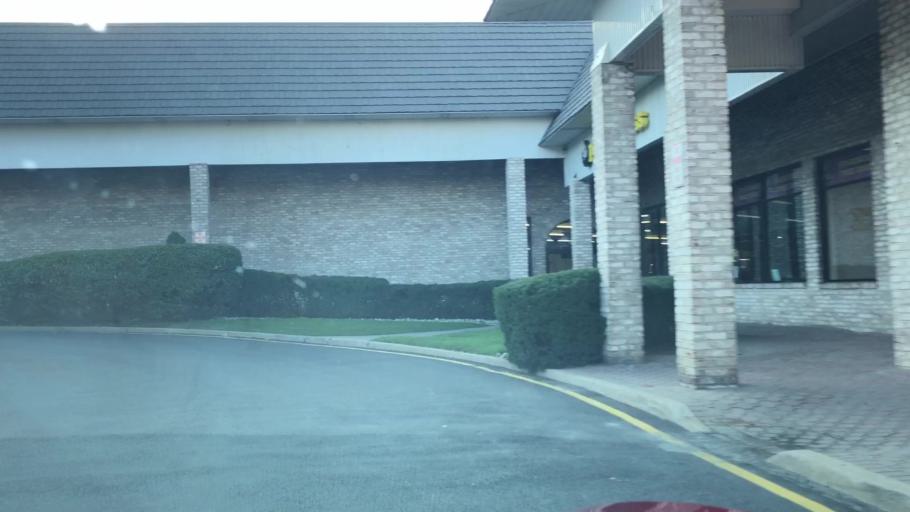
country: US
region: New Jersey
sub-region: Morris County
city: Morris Plains
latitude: 40.8616
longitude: -74.4929
